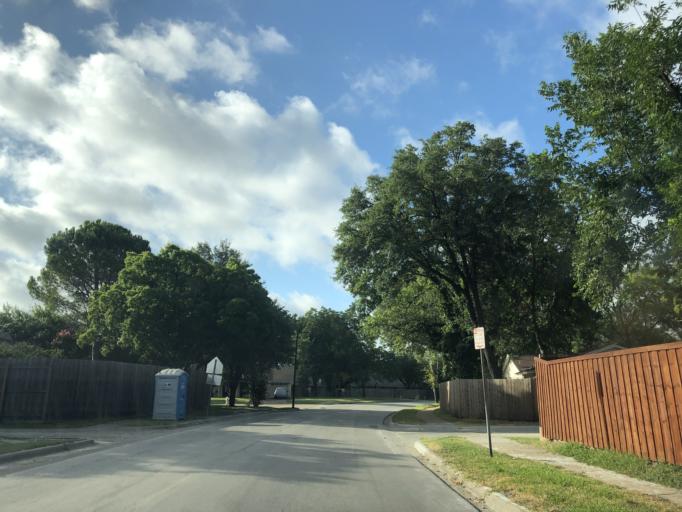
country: US
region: Texas
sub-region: Dallas County
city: Garland
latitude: 32.8539
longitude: -96.6389
